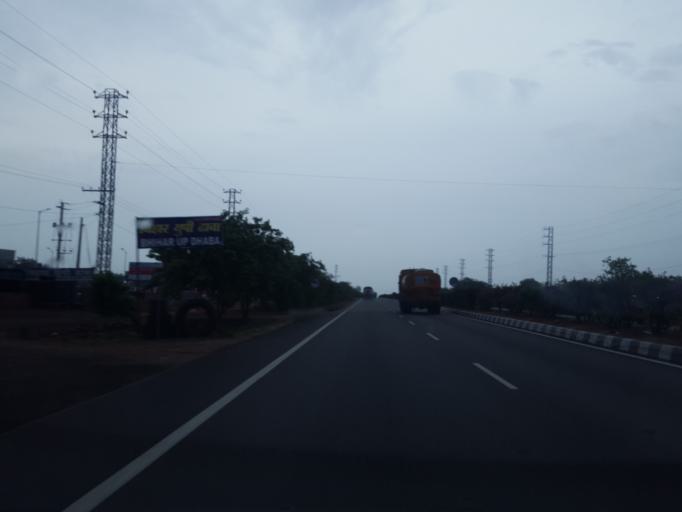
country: IN
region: Telangana
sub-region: Mahbubnagar
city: Farrukhnagar
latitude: 17.1310
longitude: 78.2811
